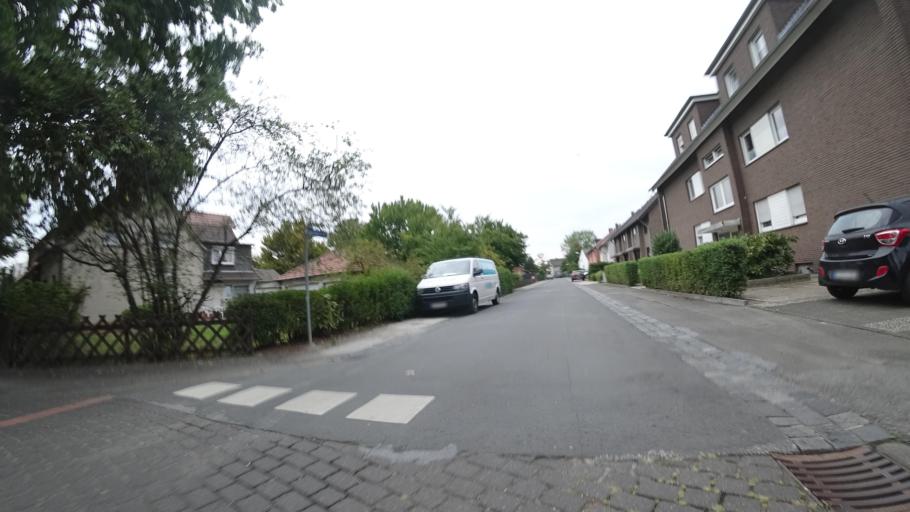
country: DE
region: North Rhine-Westphalia
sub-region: Regierungsbezirk Detmold
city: Guetersloh
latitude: 51.9140
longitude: 8.4123
